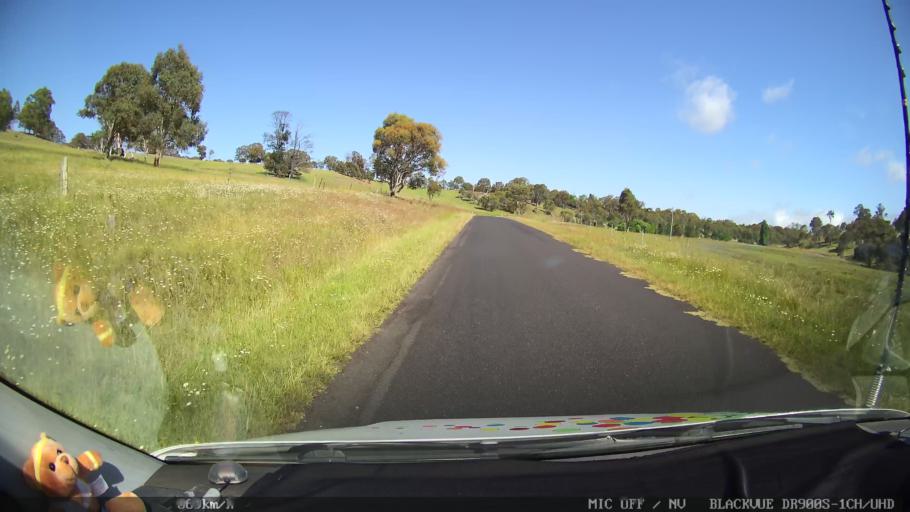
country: AU
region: New South Wales
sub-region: Guyra
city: Guyra
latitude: -30.1146
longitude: 151.6857
